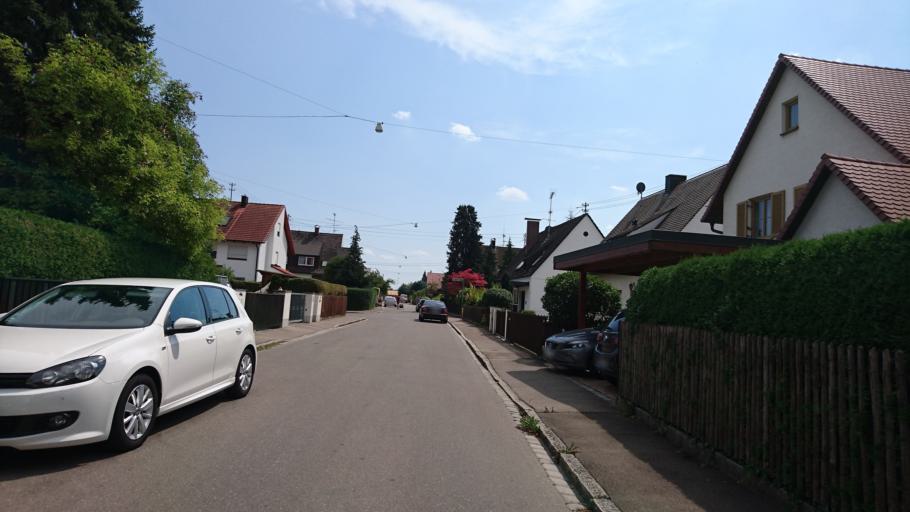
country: DE
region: Bavaria
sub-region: Swabia
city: Augsburg
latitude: 48.3894
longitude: 10.9244
